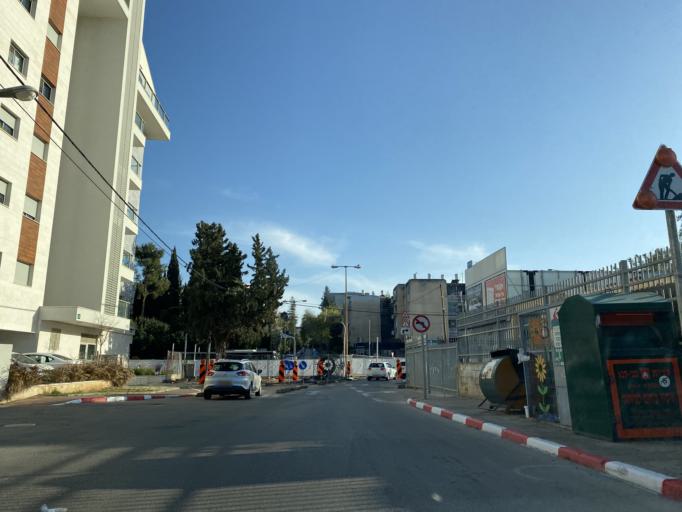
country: IL
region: Central District
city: Kfar Saba
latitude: 32.1742
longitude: 34.9156
